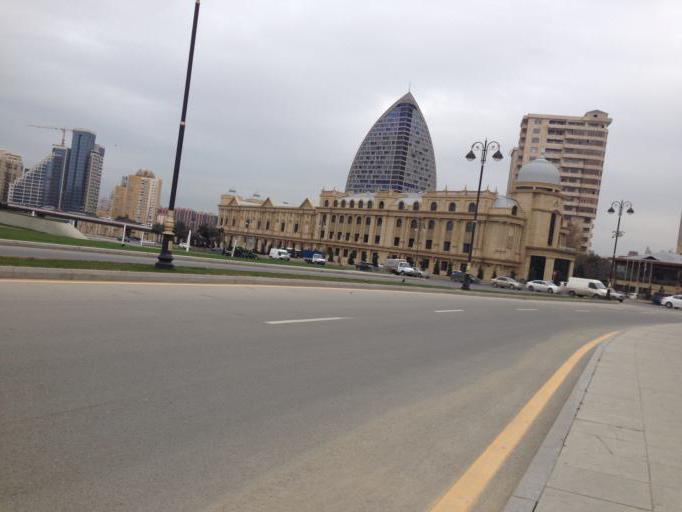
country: AZ
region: Baki
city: Baku
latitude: 40.3937
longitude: 49.8643
